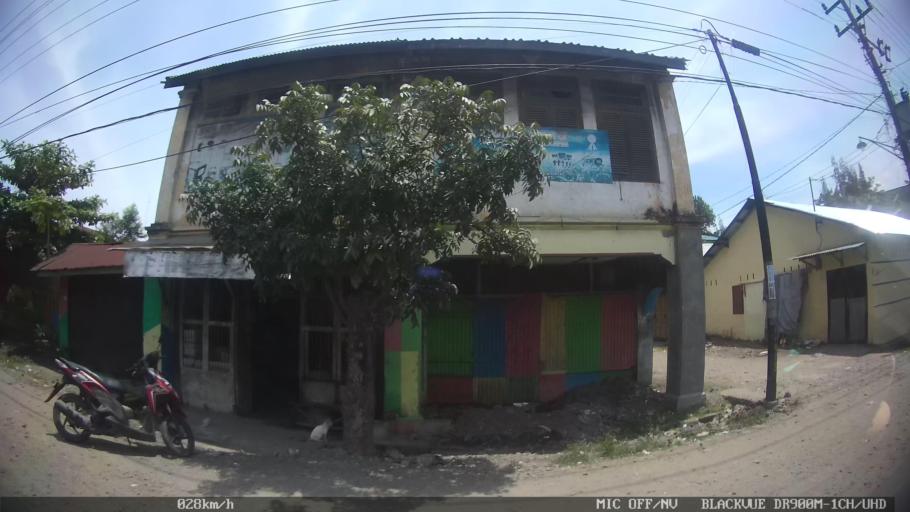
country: ID
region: North Sumatra
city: Labuhan Deli
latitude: 3.7415
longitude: 98.6751
